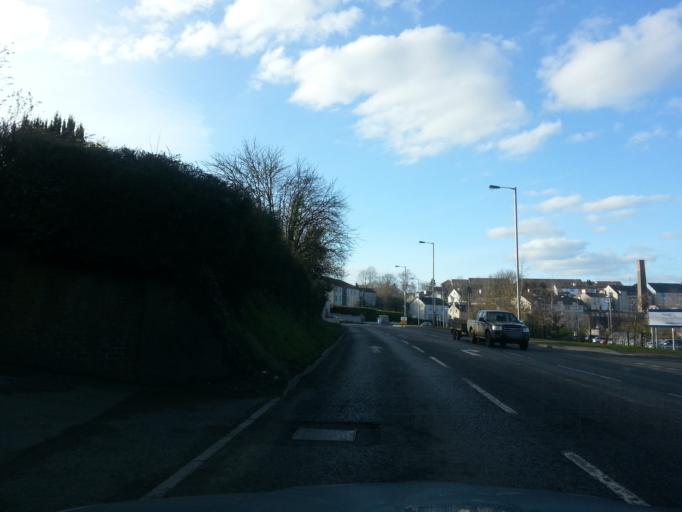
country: GB
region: Northern Ireland
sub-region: Fermanagh District
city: Enniskillen
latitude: 54.3428
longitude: -7.6487
